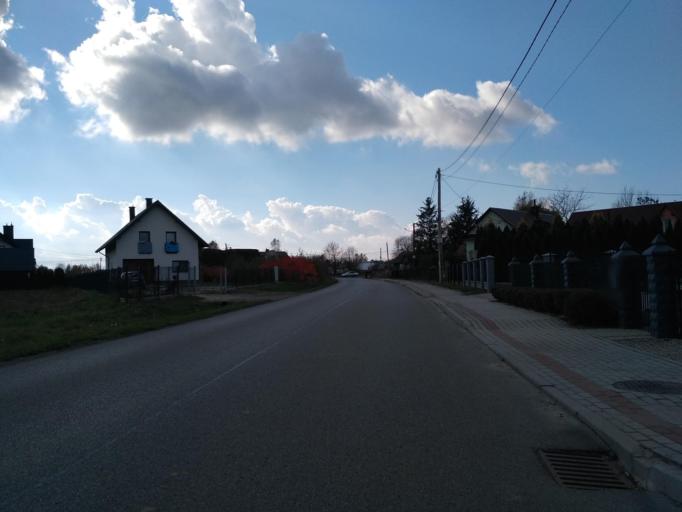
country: PL
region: Subcarpathian Voivodeship
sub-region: Powiat rzeszowski
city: Swilcza
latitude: 50.1150
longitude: 21.8751
